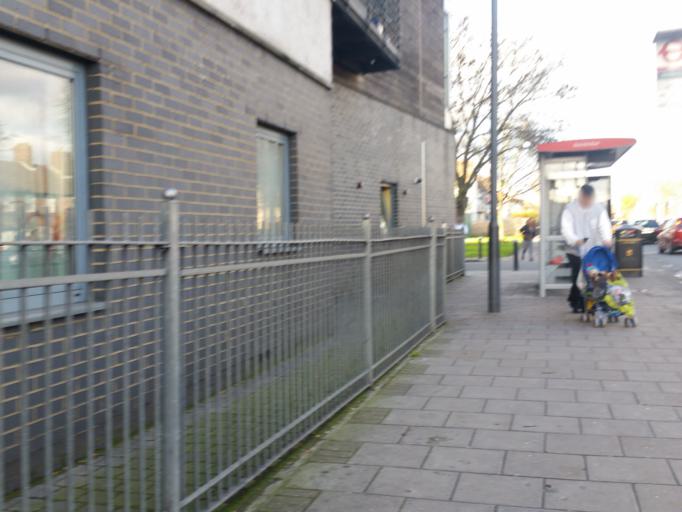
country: GB
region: England
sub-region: Greater London
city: Harringay
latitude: 51.5988
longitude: -0.0922
